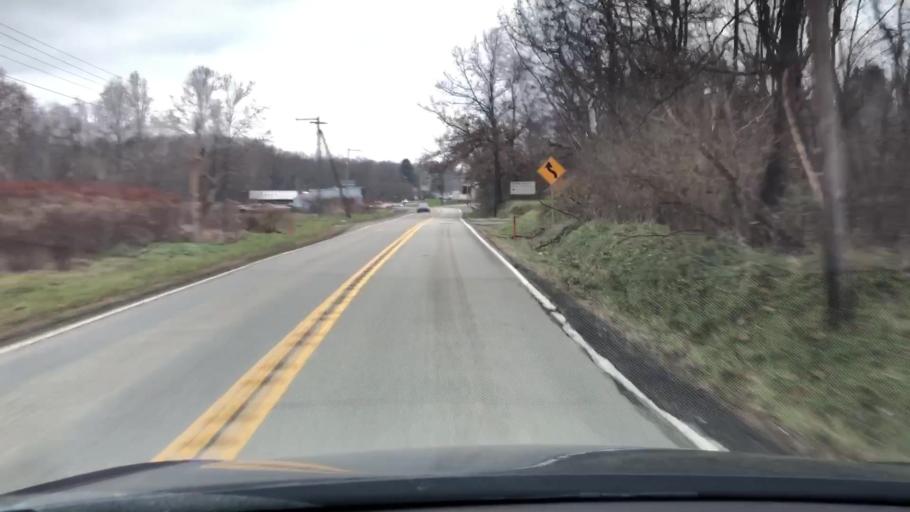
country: US
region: Pennsylvania
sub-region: Westmoreland County
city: New Stanton
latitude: 40.2045
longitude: -79.6231
